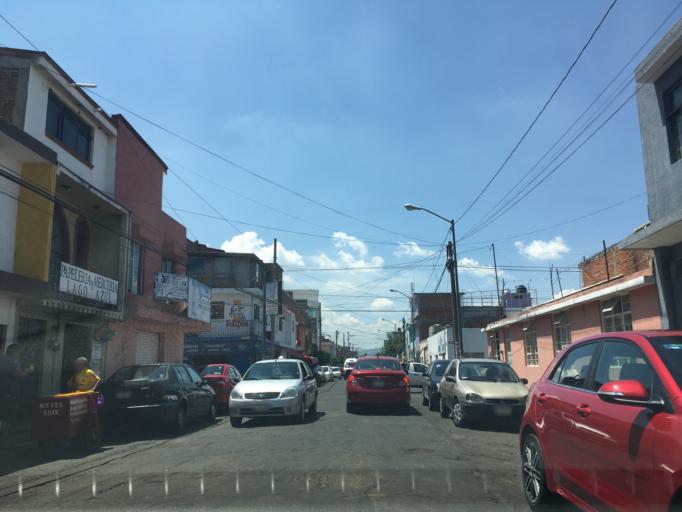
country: MX
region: Michoacan
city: Morelia
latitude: 19.6901
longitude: -101.1837
